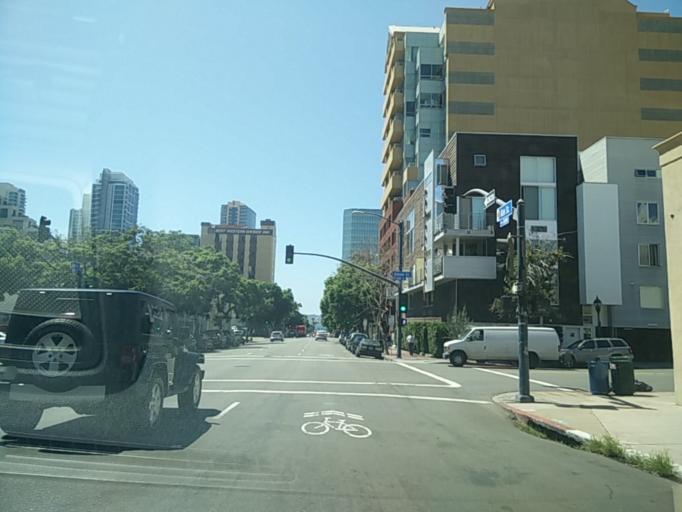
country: US
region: California
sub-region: San Diego County
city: San Diego
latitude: 32.7200
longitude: -117.1653
